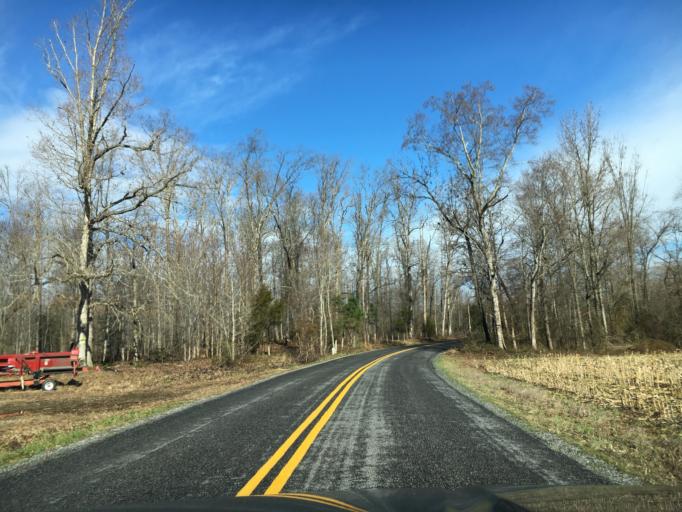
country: US
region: Virginia
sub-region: Amelia County
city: Amelia Court House
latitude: 37.4246
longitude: -78.0675
